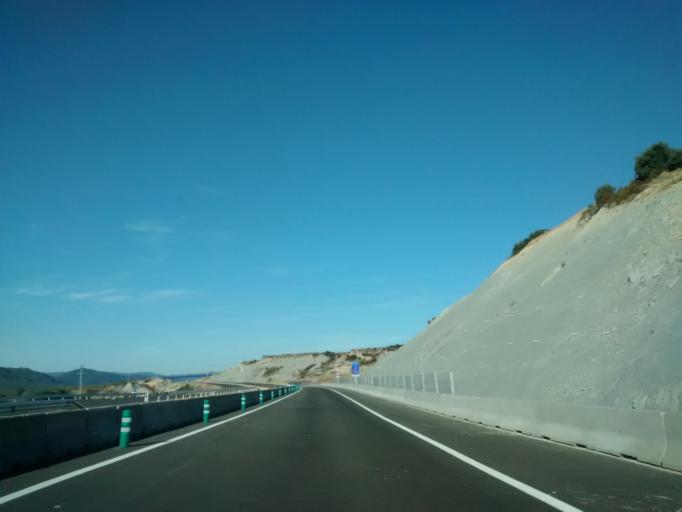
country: ES
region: Aragon
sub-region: Provincia de Huesca
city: Santa Cruz de la Seros
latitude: 42.5649
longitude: -0.7091
